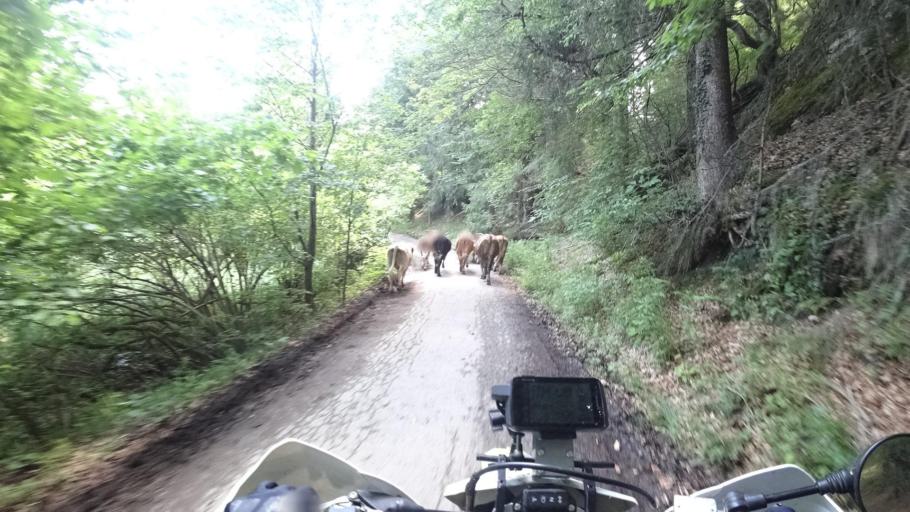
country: HR
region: Licko-Senjska
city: Jezerce
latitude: 44.8445
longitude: 15.5994
